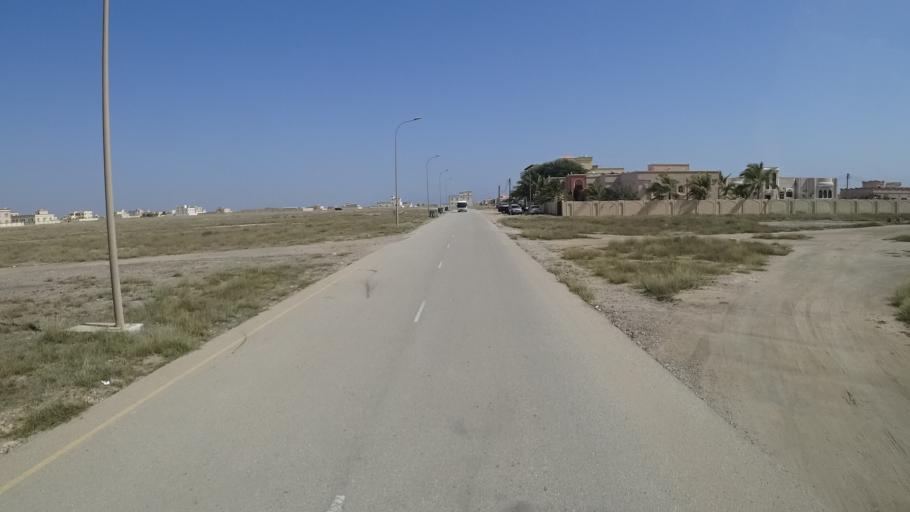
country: OM
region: Zufar
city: Salalah
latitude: 16.9857
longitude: 54.7092
